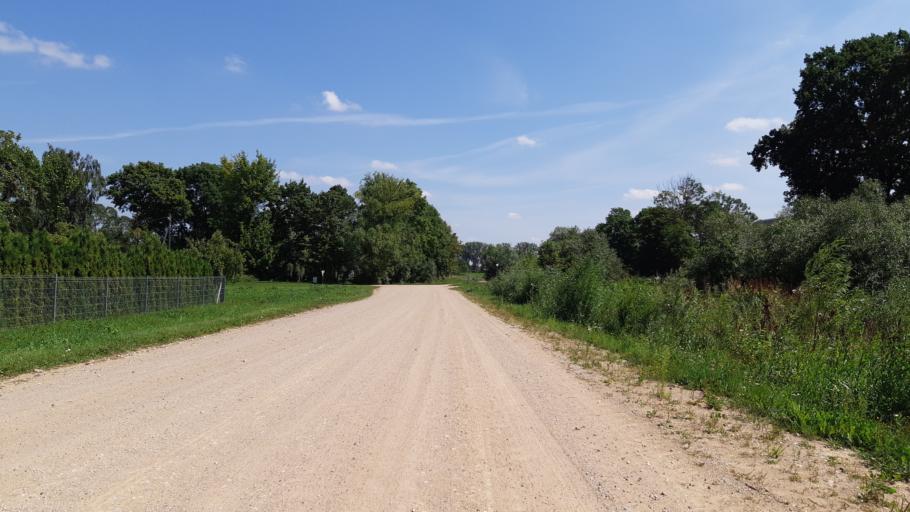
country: LT
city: Virbalis
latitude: 54.6233
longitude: 22.8186
